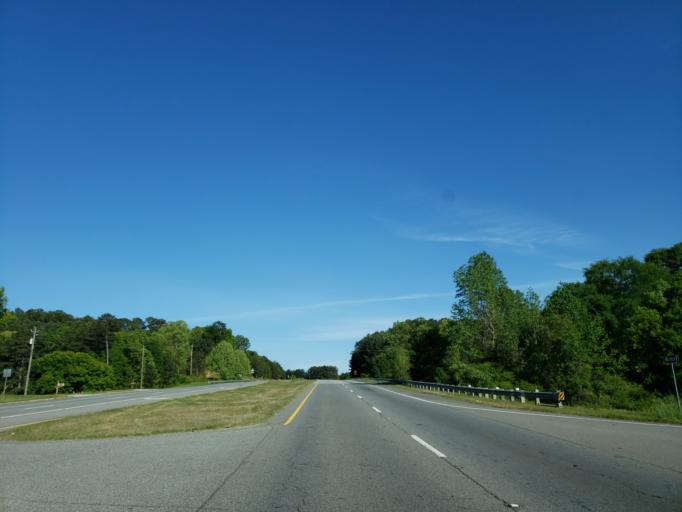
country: US
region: Georgia
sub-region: Polk County
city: Cedartown
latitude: 34.0118
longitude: -85.1832
